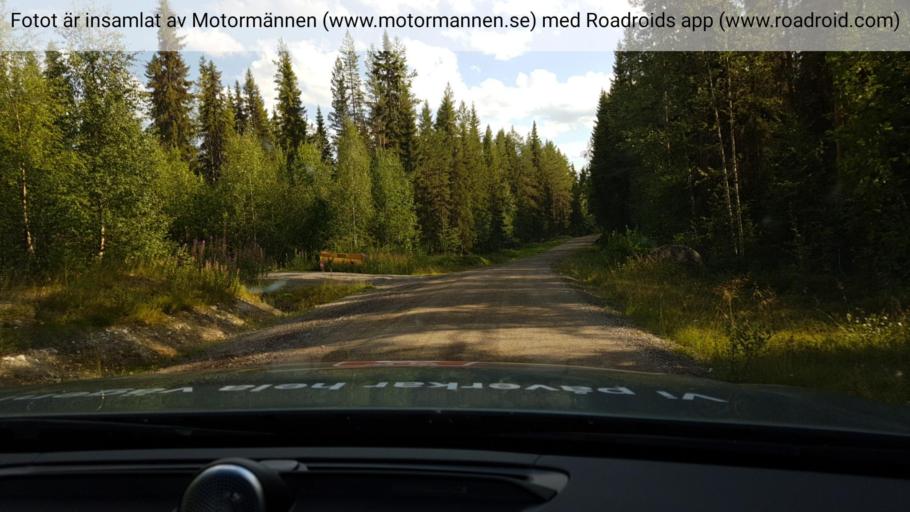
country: SE
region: Vaesterbotten
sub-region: Dorotea Kommun
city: Dorotea
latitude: 63.9543
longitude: 16.0781
